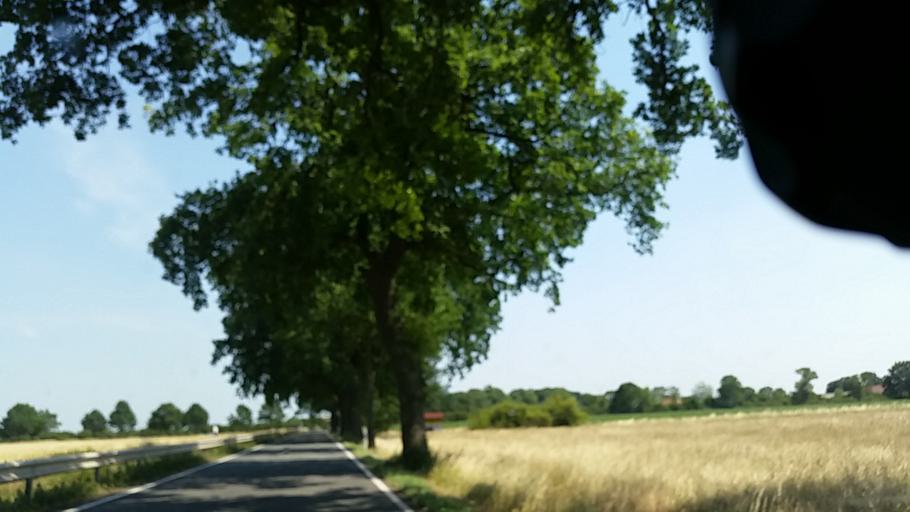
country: DE
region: Lower Saxony
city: Thedinghausen
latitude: 52.9844
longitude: 9.0034
